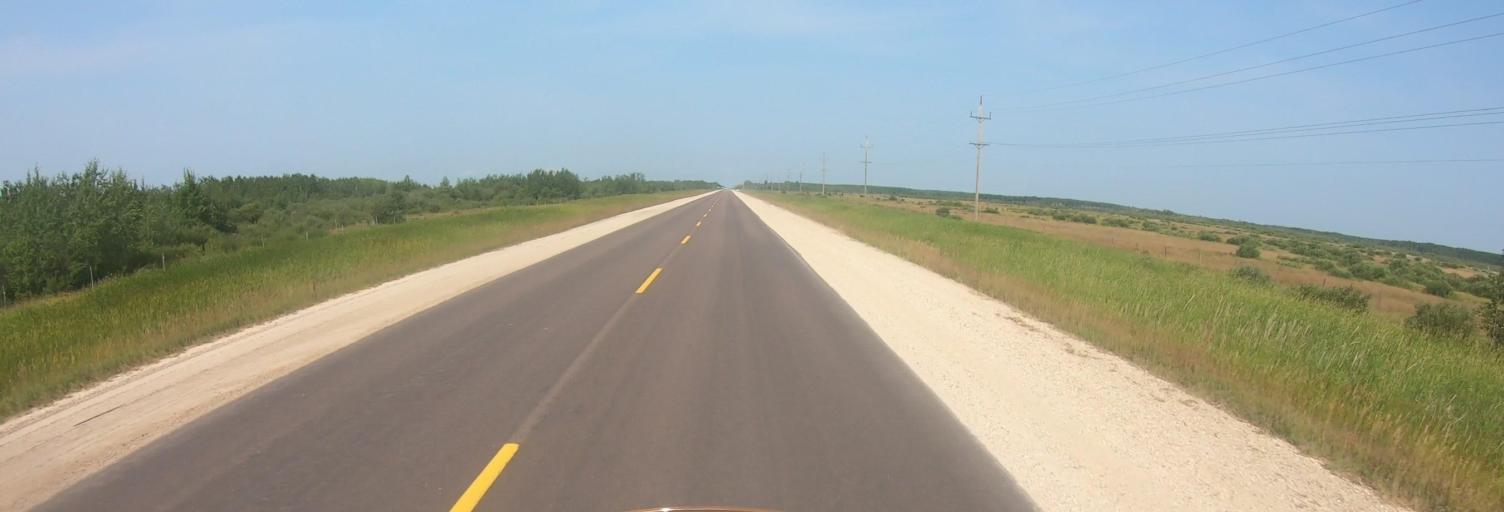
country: CA
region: Manitoba
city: La Broquerie
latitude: 49.2757
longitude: -96.4934
